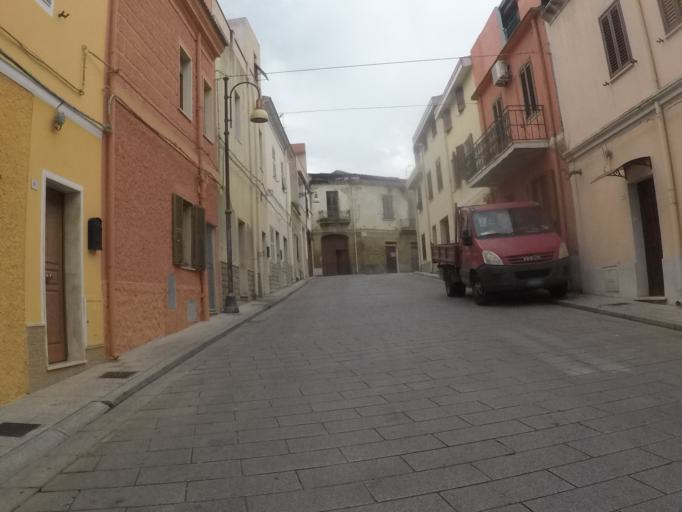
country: IT
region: Sardinia
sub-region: Provincia di Sassari
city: Sorso
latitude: 40.7981
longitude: 8.5815
